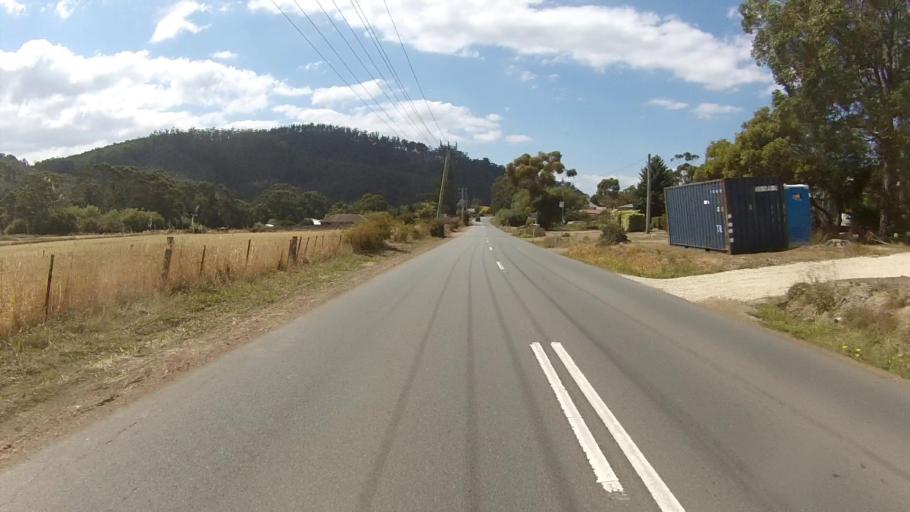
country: AU
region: Tasmania
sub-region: Clarence
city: Cambridge
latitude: -42.8406
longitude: 147.4226
